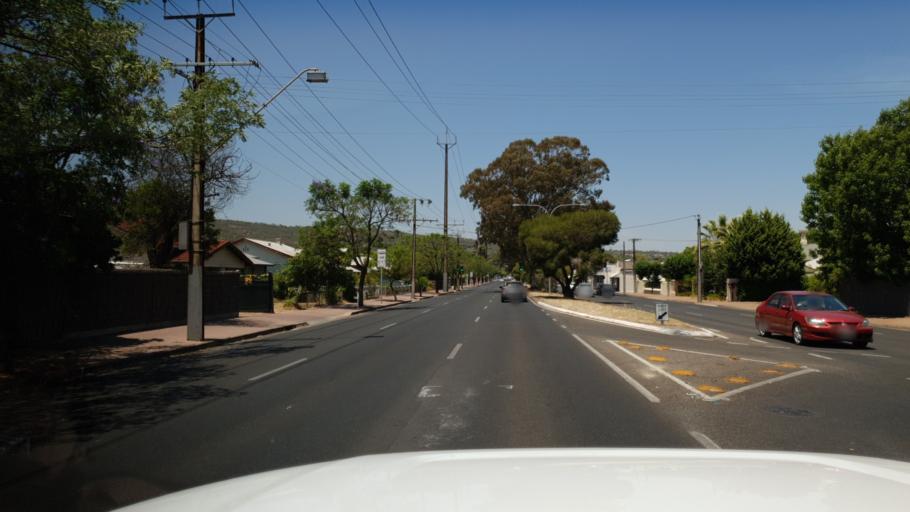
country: AU
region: South Australia
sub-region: Mitcham
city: Clapham
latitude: -34.9856
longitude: 138.5923
